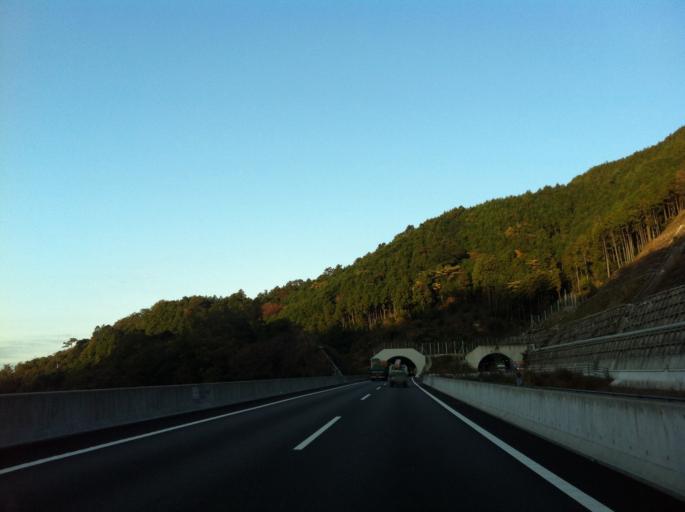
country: JP
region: Aichi
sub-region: Tokai-shi
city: Toyokawa
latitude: 34.8823
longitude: 137.3833
